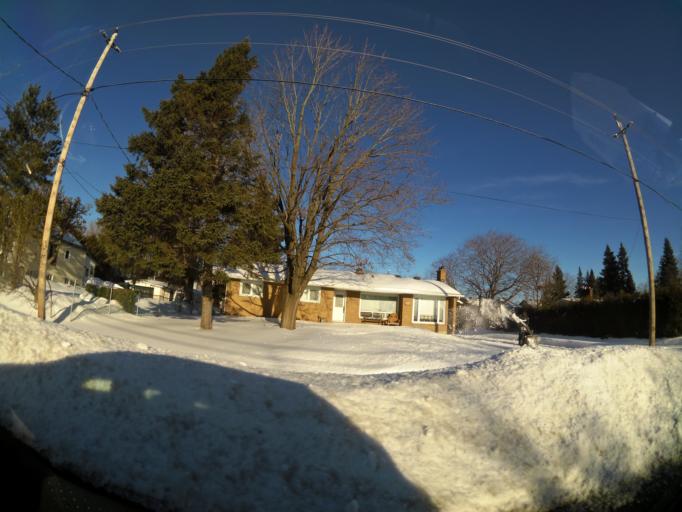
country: CA
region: Ontario
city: Ottawa
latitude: 45.4320
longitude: -75.5185
